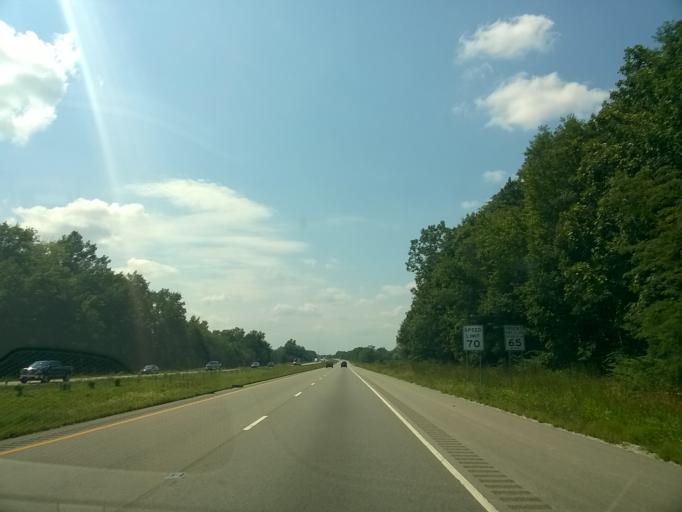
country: US
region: Indiana
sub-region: Morgan County
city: Monrovia
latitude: 39.6092
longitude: -86.4942
